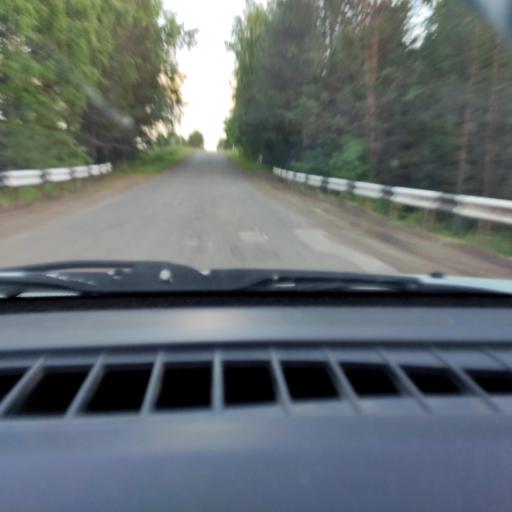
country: RU
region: Perm
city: Kukushtan
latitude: 57.2986
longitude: 56.5373
